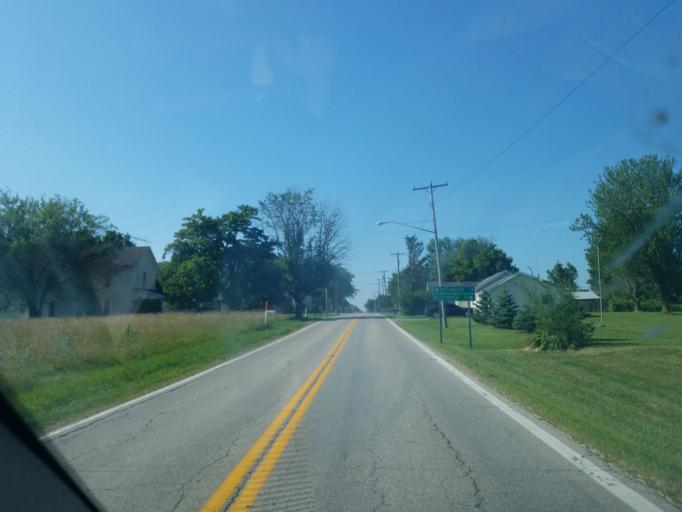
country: US
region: Ohio
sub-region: Union County
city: Richwood
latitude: 40.4097
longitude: -83.4531
